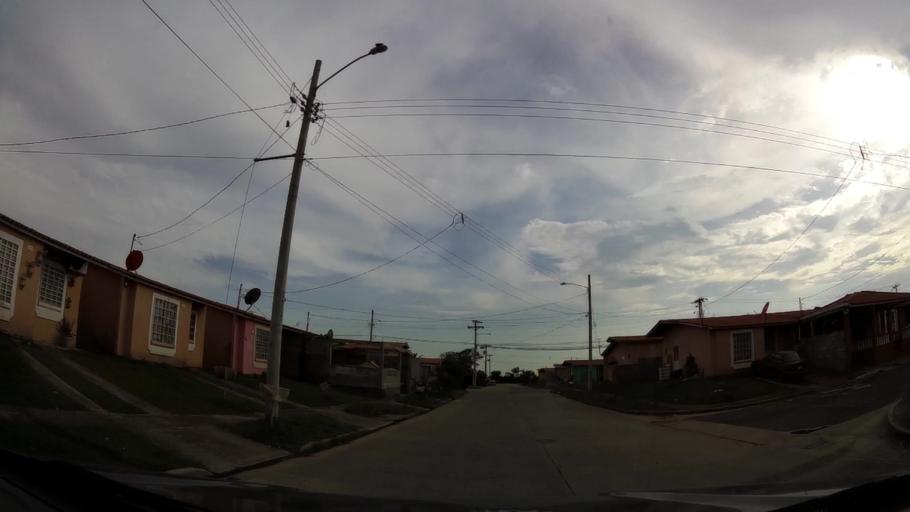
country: PA
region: Panama
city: Tocumen
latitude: 9.0696
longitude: -79.3619
